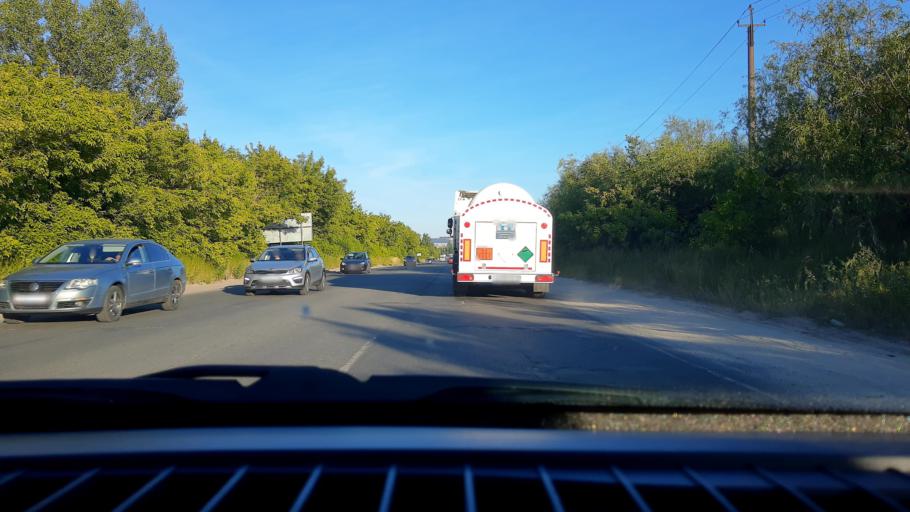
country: RU
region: Nizjnij Novgorod
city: Dzerzhinsk
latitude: 56.2498
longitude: 43.4969
